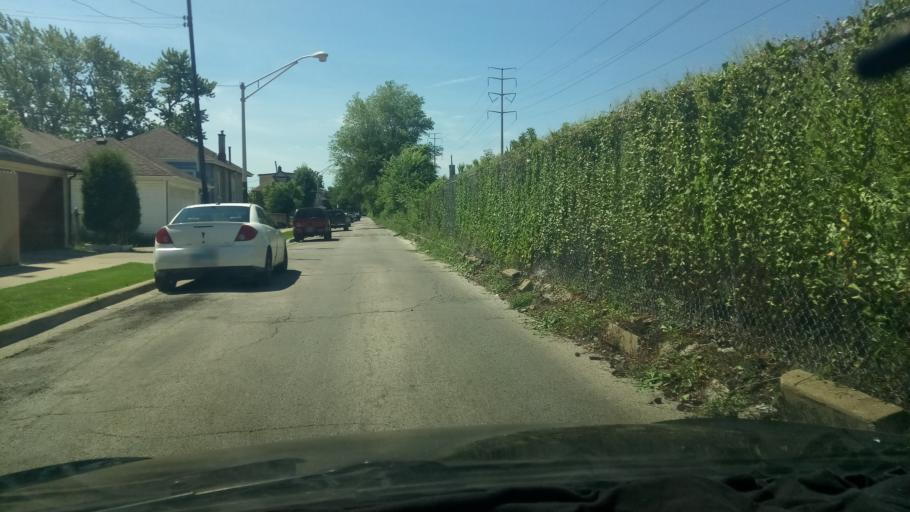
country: US
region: Illinois
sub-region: Cook County
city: Hometown
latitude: 41.7752
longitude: -87.7125
